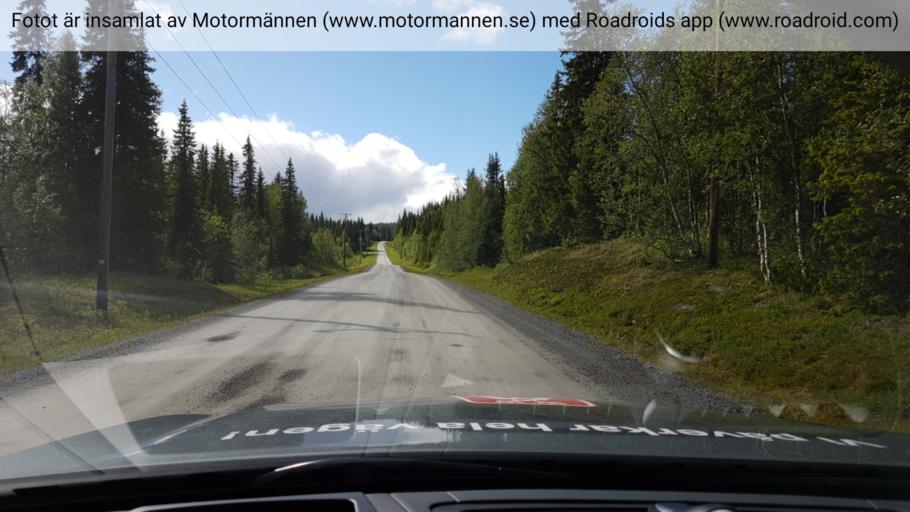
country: SE
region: Jaemtland
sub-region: Are Kommun
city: Are
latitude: 63.6733
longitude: 12.8390
